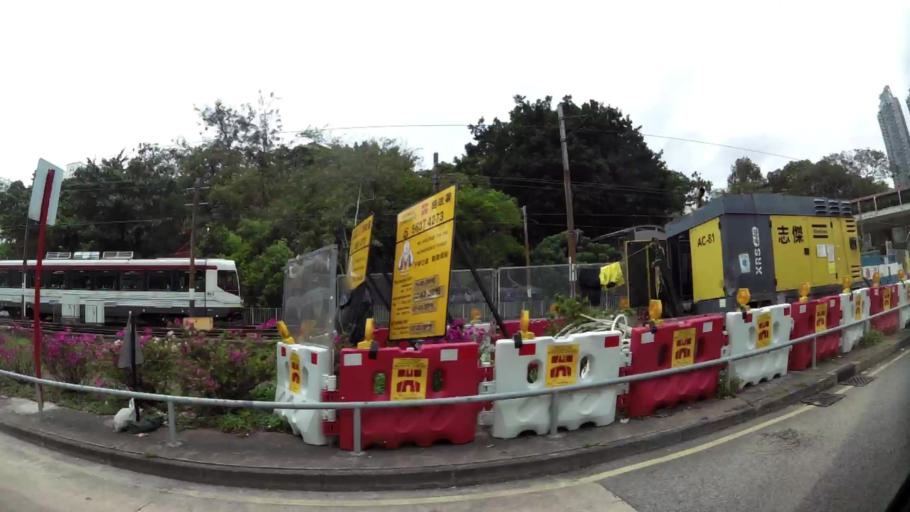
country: HK
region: Tuen Mun
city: Tuen Mun
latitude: 22.3906
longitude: 113.9751
